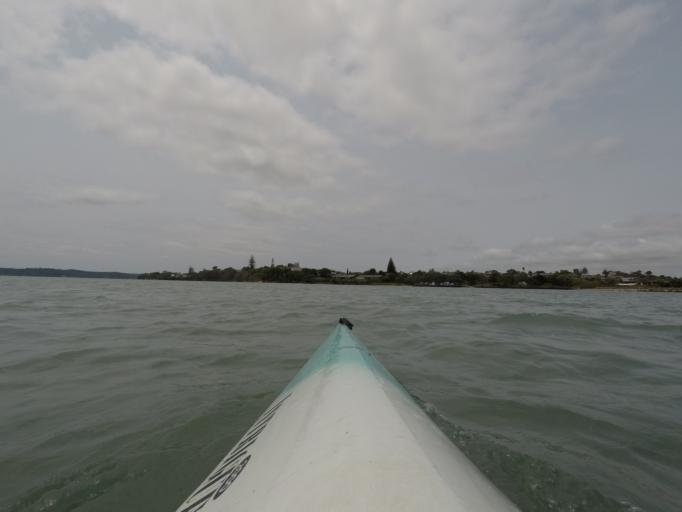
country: NZ
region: Auckland
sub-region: Auckland
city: Rosebank
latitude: -36.8704
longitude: 174.6943
